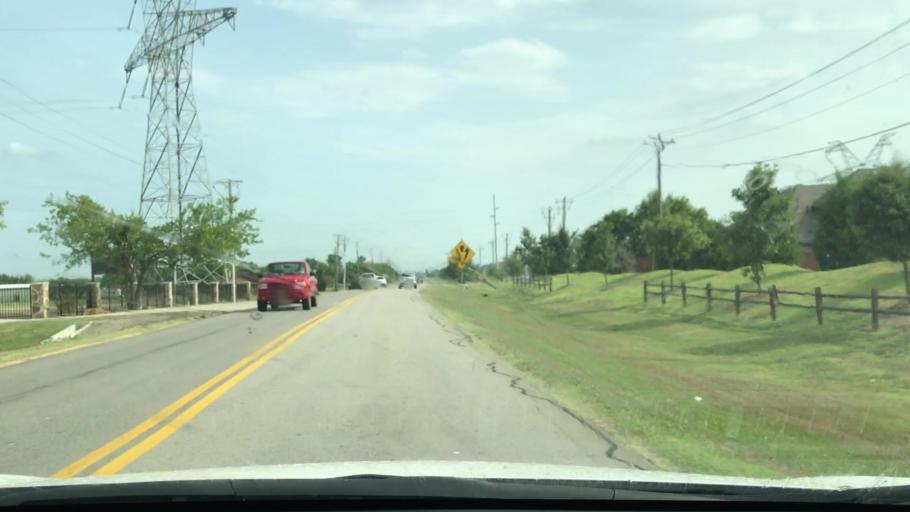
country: US
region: Texas
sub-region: Collin County
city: Wylie
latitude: 32.9929
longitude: -96.5216
